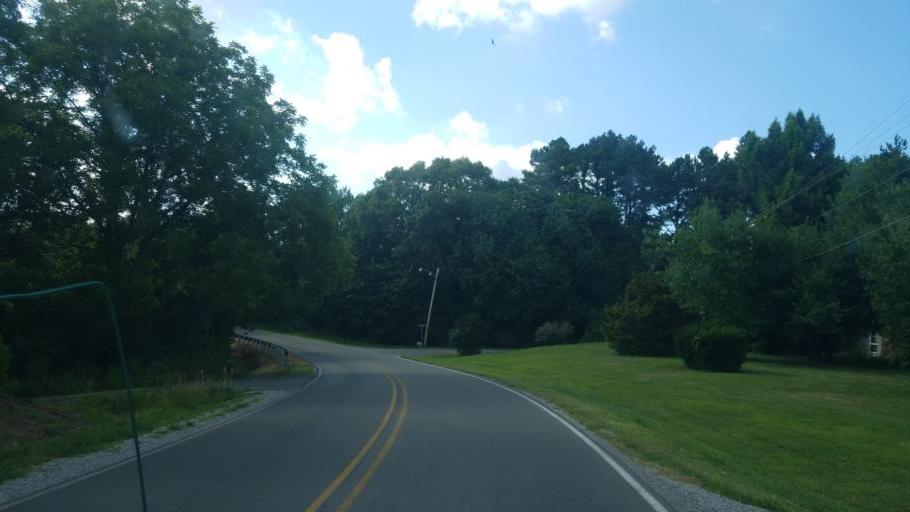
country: US
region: Illinois
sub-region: Union County
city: Cobden
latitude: 37.5679
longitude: -89.3121
